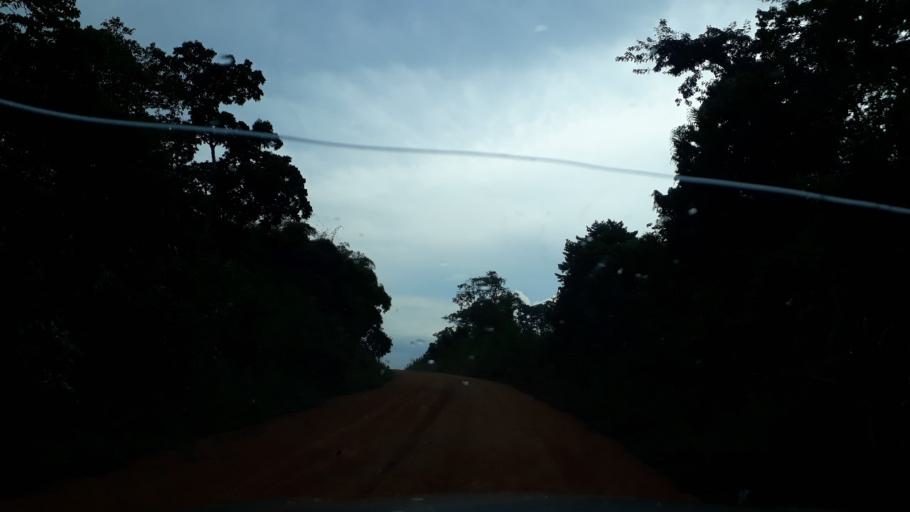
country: CD
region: Eastern Province
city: Bunia
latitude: 1.4001
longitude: 29.3998
